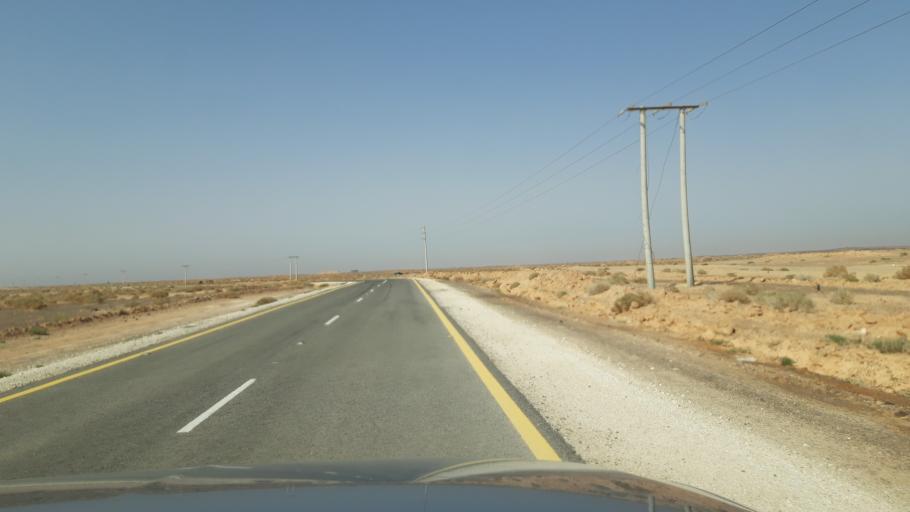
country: JO
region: Amman
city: Al Azraq ash Shamali
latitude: 31.7775
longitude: 36.7742
